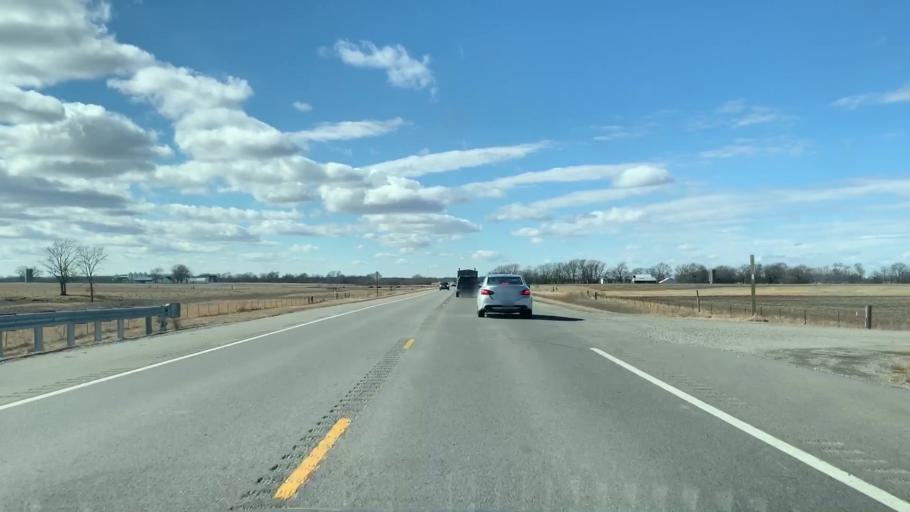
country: US
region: Kansas
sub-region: Crawford County
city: Pittsburg
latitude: 37.3396
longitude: -94.8508
